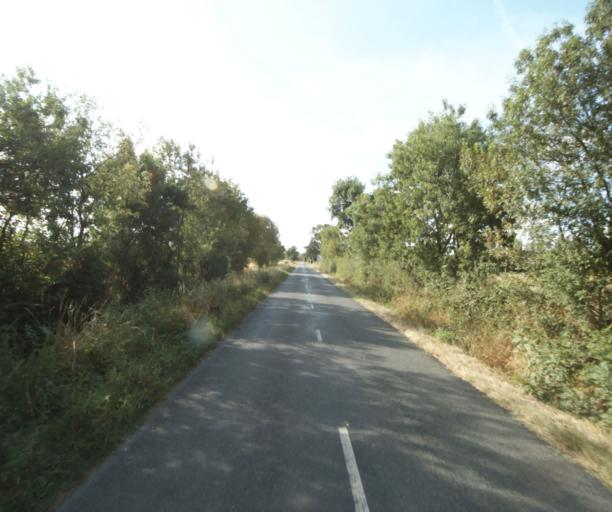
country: FR
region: Midi-Pyrenees
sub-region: Departement de la Haute-Garonne
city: Revel
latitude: 43.4870
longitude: 1.9832
